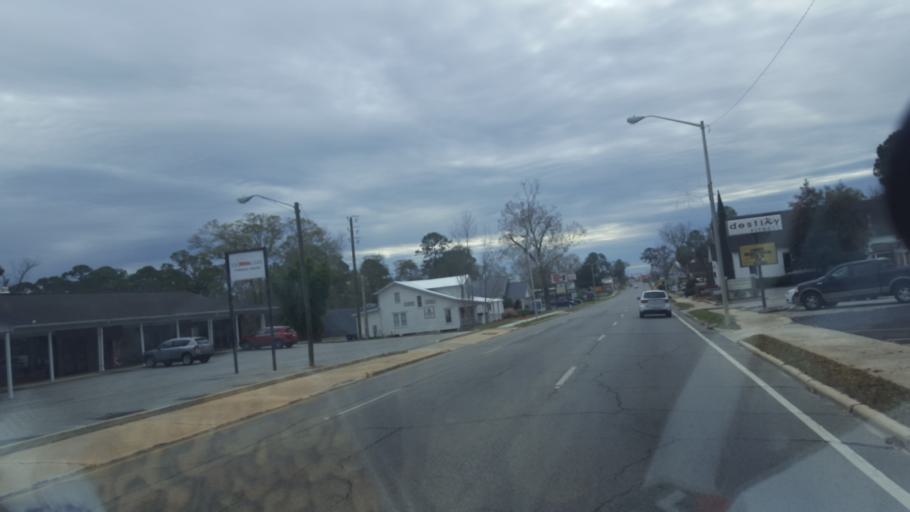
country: US
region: Georgia
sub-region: Ben Hill County
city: Fitzgerald
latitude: 31.7113
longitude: -83.2529
